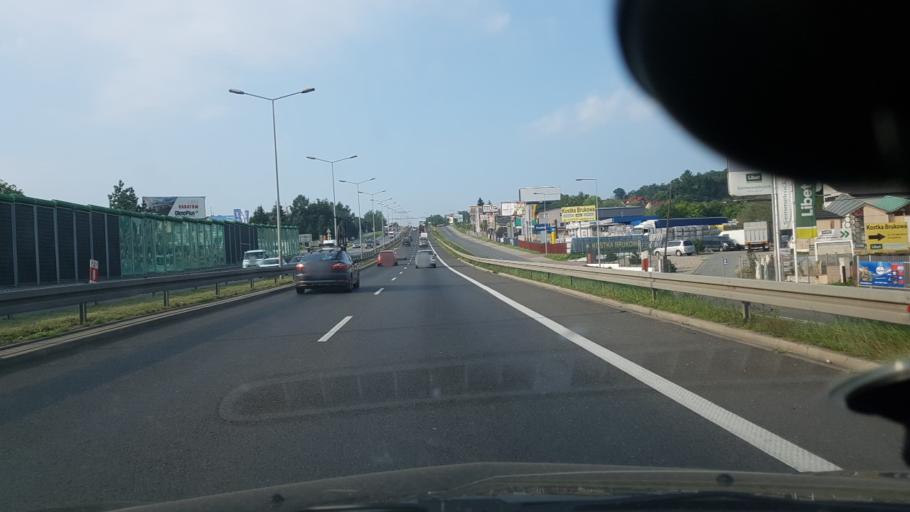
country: PL
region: Lesser Poland Voivodeship
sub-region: Powiat krakowski
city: Libertow
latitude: 49.9779
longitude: 19.9095
